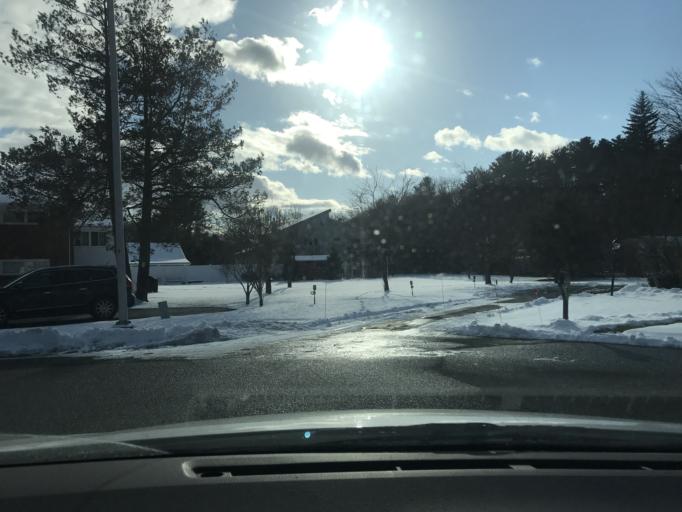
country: US
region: Massachusetts
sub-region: Essex County
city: Saugus
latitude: 42.4958
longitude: -71.0220
